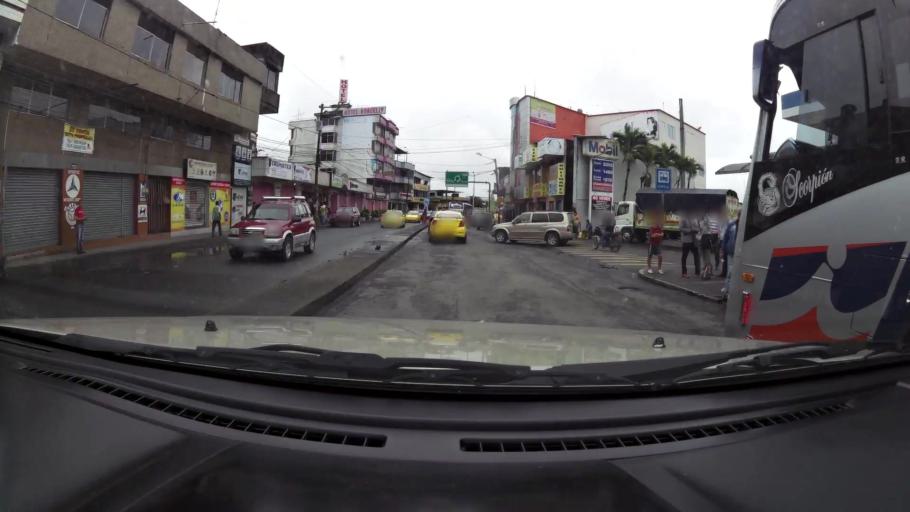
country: EC
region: Santo Domingo de los Tsachilas
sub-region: Canton Santo Domingo de los Colorados
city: Santo Domingo de los Colorados
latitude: -0.2548
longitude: -79.1765
